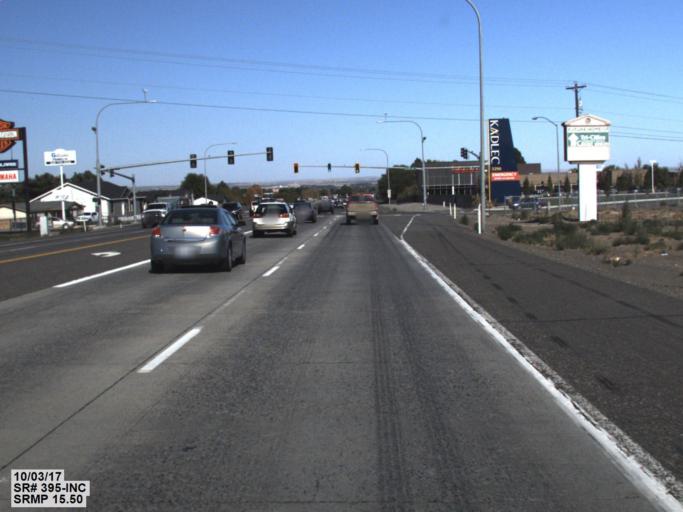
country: US
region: Washington
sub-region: Benton County
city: Kennewick
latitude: 46.1911
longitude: -119.1679
